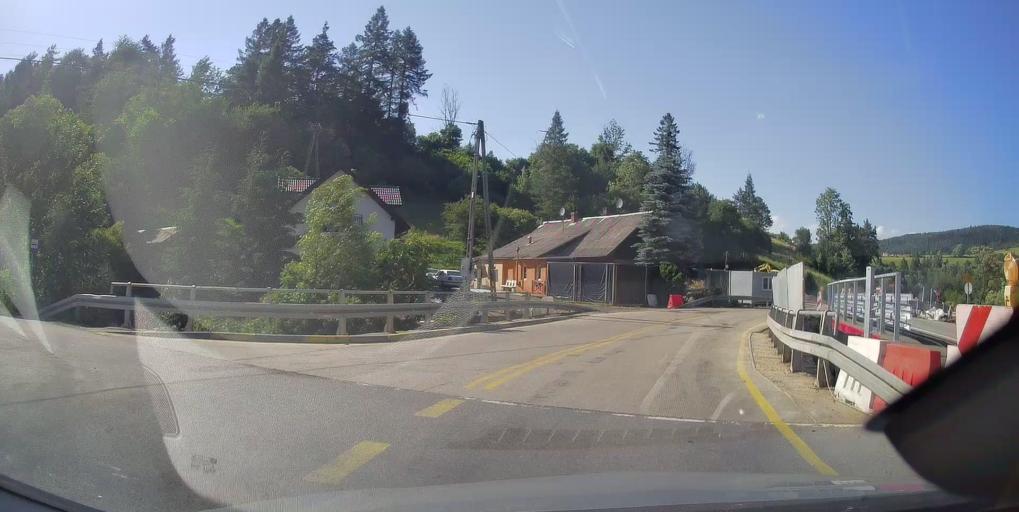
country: PL
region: Lesser Poland Voivodeship
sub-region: Powiat nowosadecki
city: Labowa
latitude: 49.4856
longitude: 20.9149
